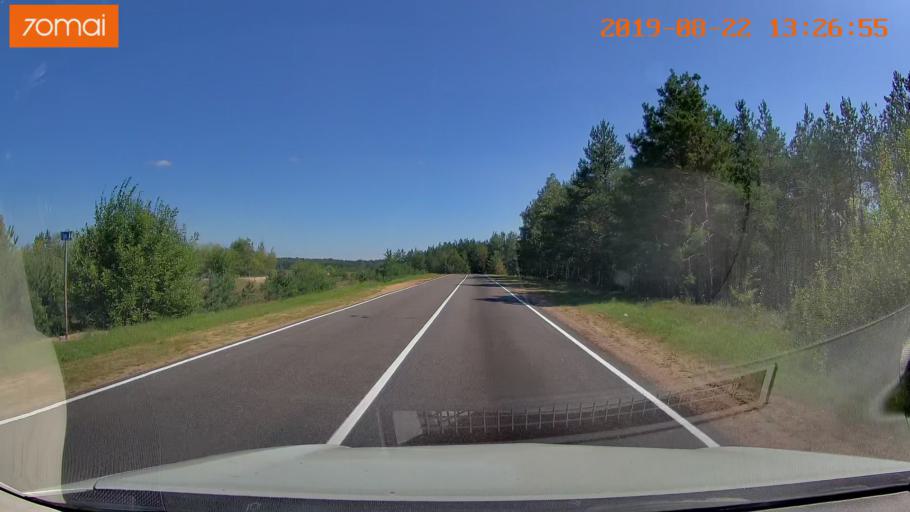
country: BY
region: Minsk
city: Staryya Darohi
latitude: 53.2073
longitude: 28.0732
